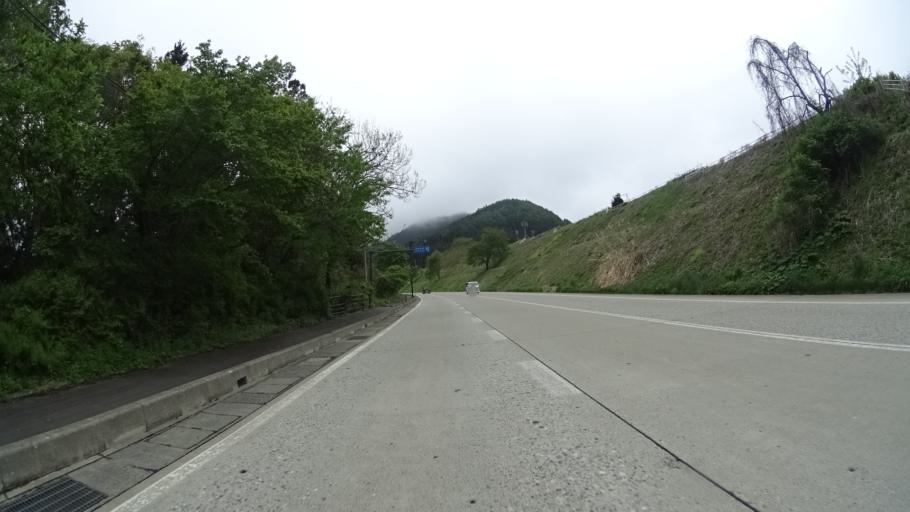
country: JP
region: Nagano
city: Nakano
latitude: 36.7329
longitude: 138.4204
